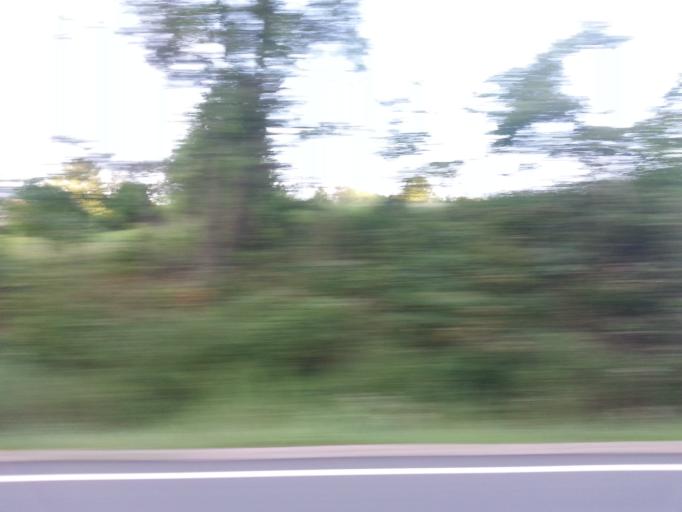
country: US
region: Tennessee
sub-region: Johnson County
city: Mountain City
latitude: 36.5395
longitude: -81.8949
